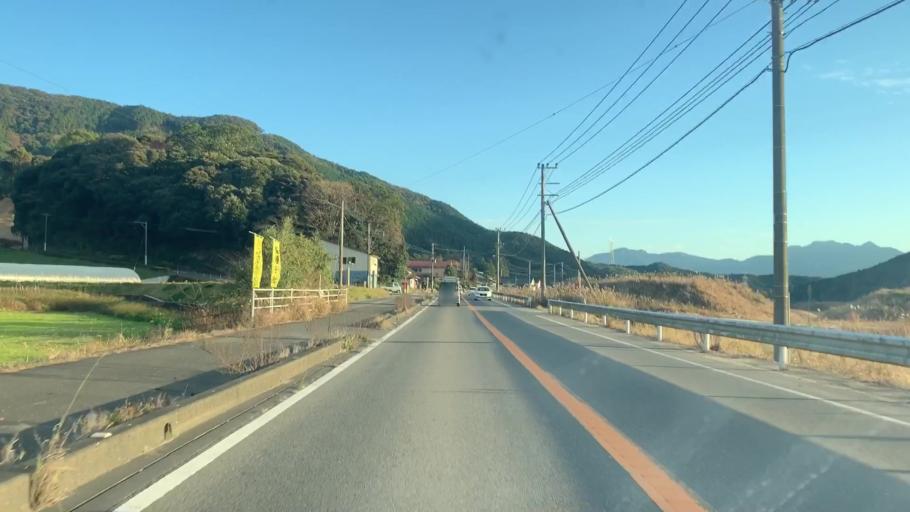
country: JP
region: Saga Prefecture
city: Karatsu
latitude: 33.3737
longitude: 130.0014
